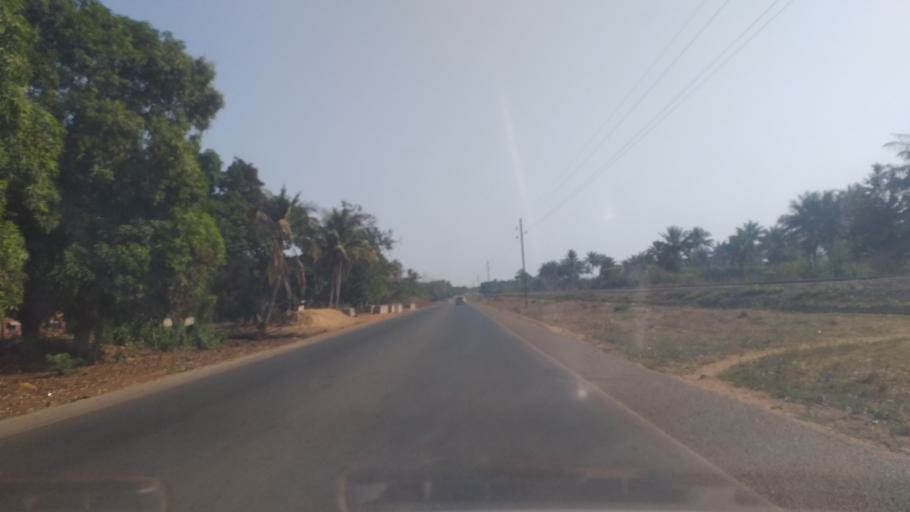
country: GN
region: Boke
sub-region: Boke Prefecture
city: Kamsar
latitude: 10.7260
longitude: -14.5189
